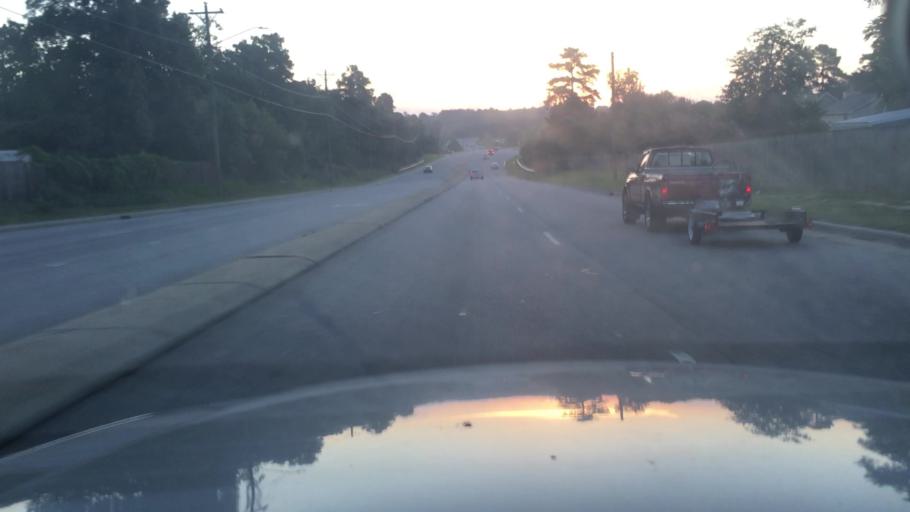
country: US
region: North Carolina
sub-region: Hoke County
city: Rockfish
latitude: 35.0612
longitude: -79.0440
